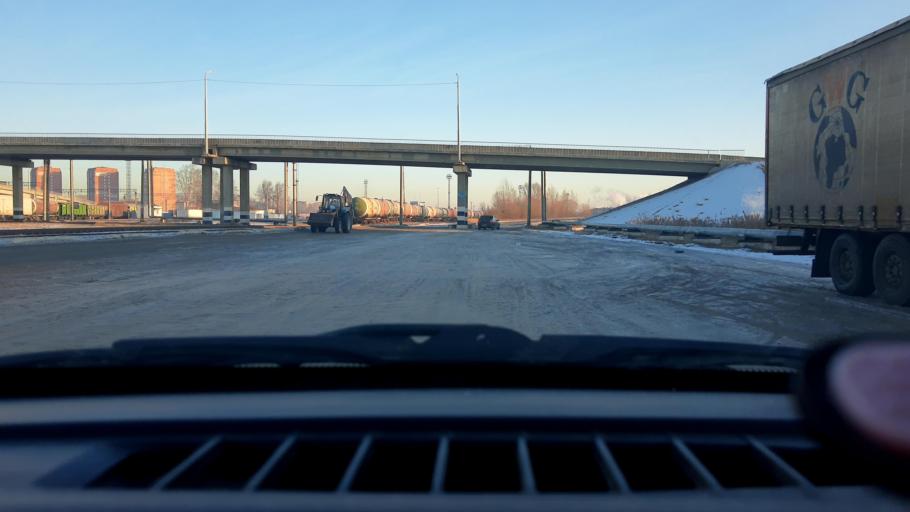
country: RU
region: Nizjnij Novgorod
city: Gorbatovka
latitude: 56.2796
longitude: 43.8419
